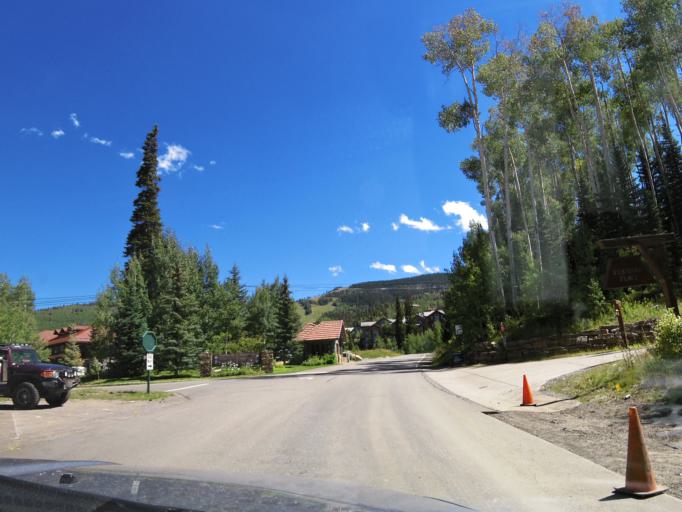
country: US
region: Colorado
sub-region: San Miguel County
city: Mountain Village
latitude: 37.9323
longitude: -107.8556
